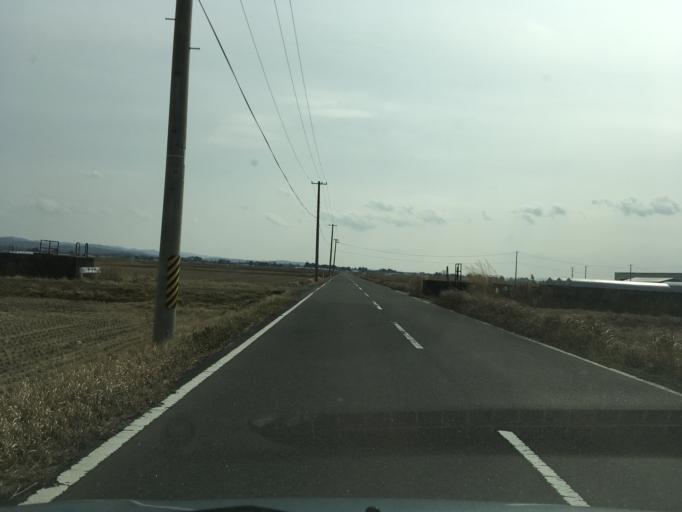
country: JP
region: Iwate
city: Ichinoseki
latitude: 38.7401
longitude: 141.2382
